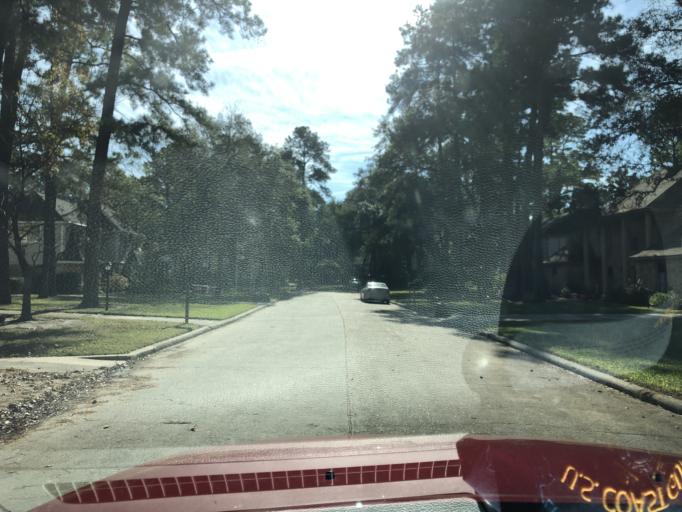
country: US
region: Texas
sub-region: Harris County
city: Tomball
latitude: 30.0296
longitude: -95.5540
